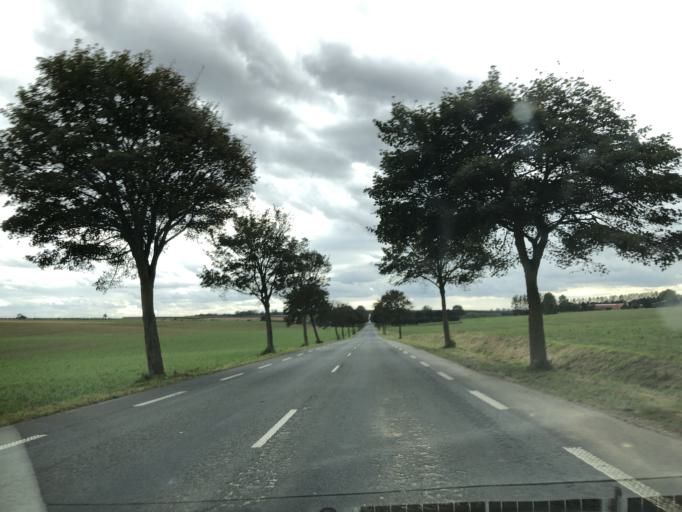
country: FR
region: Nord-Pas-de-Calais
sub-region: Departement du Pas-de-Calais
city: Auchy-les-Hesdin
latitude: 50.4407
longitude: 2.0767
